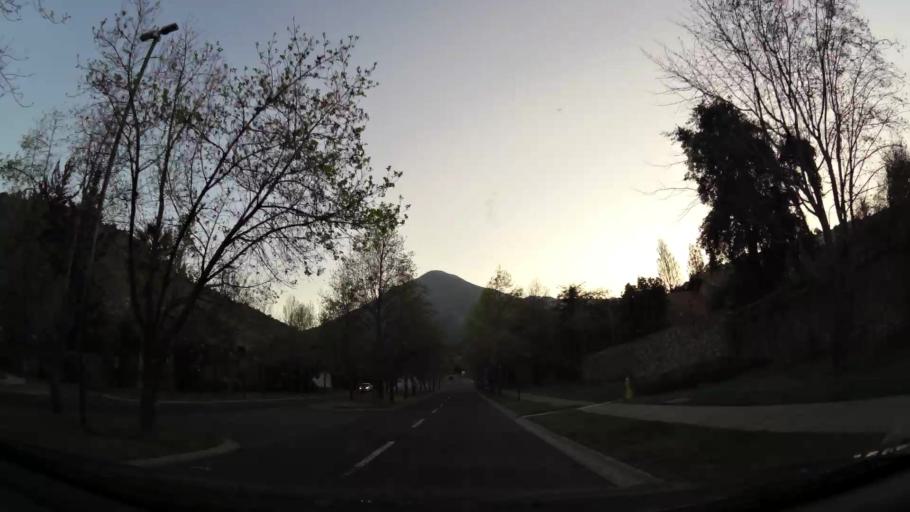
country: CL
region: Santiago Metropolitan
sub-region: Provincia de Chacabuco
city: Chicureo Abajo
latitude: -33.3406
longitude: -70.5596
